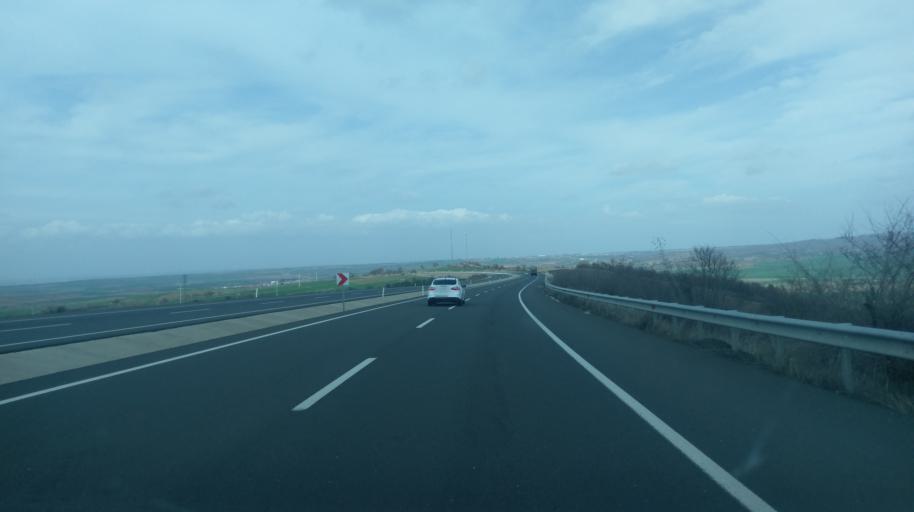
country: TR
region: Edirne
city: Hamidiye
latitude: 41.0872
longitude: 26.6399
